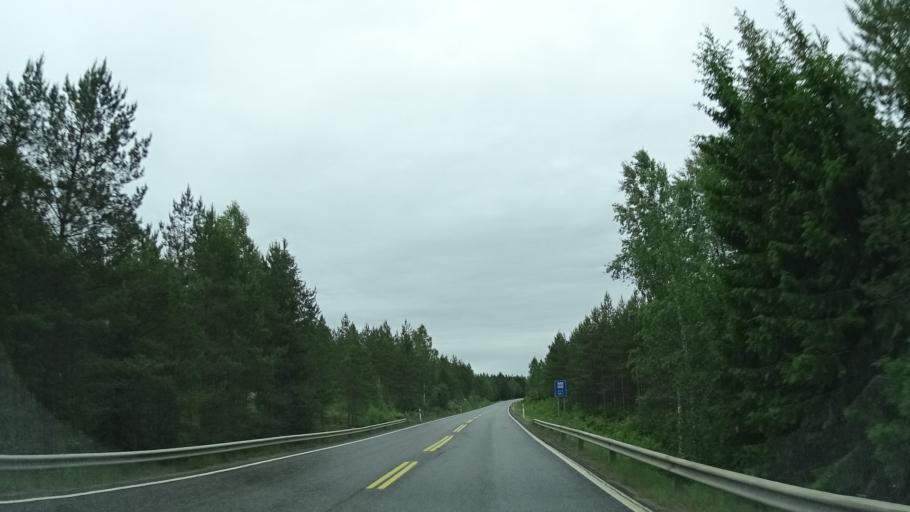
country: FI
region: Varsinais-Suomi
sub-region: Salo
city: Pernioe
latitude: 60.1205
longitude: 23.2025
